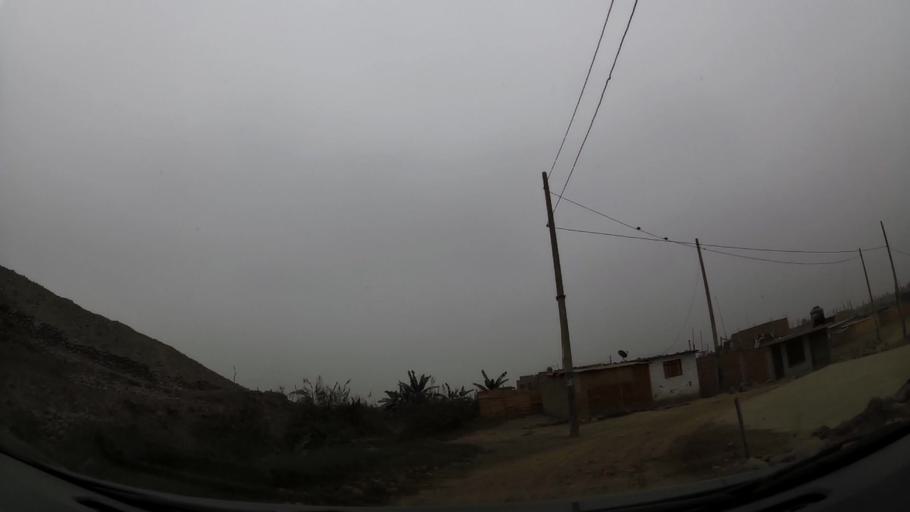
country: PE
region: Lima
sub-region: Lima
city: Carabayllo
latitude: -11.8580
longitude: -77.0202
